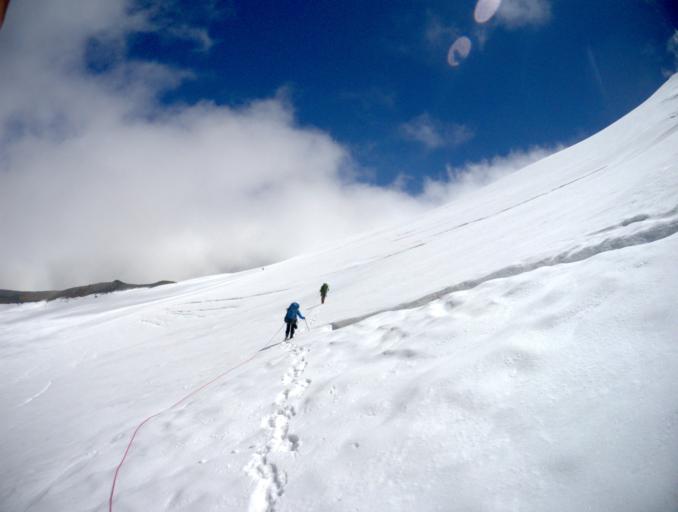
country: RU
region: Kabardino-Balkariya
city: Terskol
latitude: 43.3794
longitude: 42.4543
